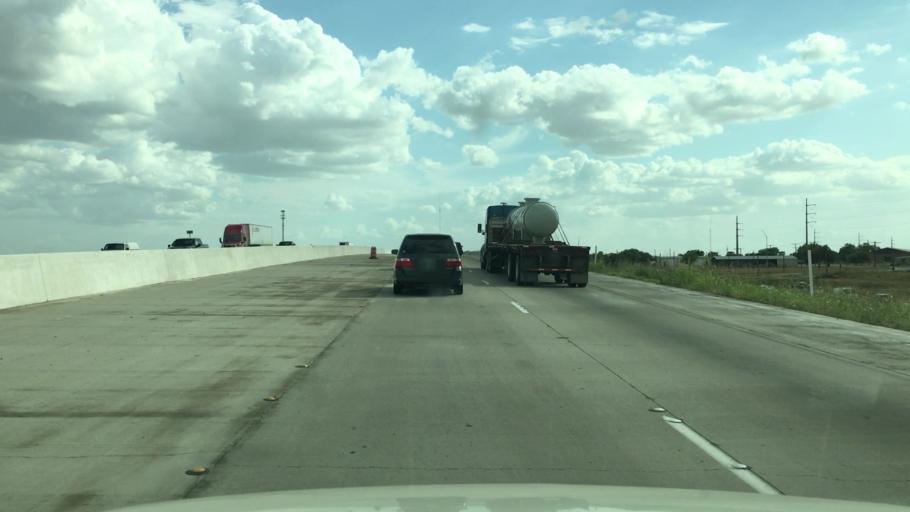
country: US
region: Texas
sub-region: McLennan County
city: Bruceville-Eddy
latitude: 31.3094
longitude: -97.2436
